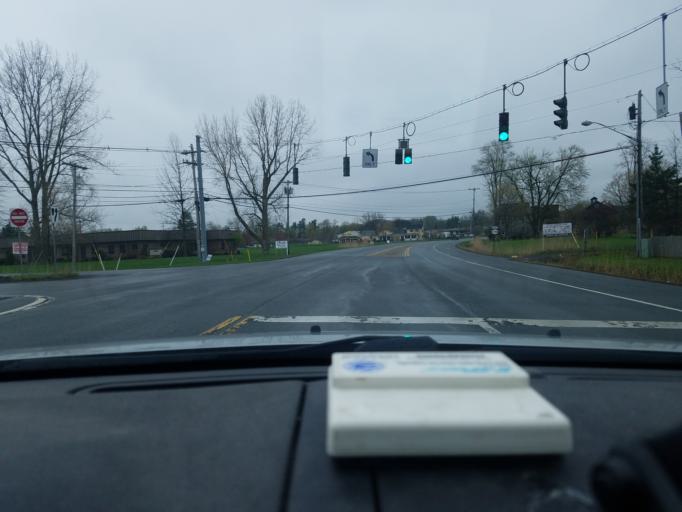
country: US
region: New York
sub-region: Onondaga County
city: East Syracuse
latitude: 43.0999
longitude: -76.0770
